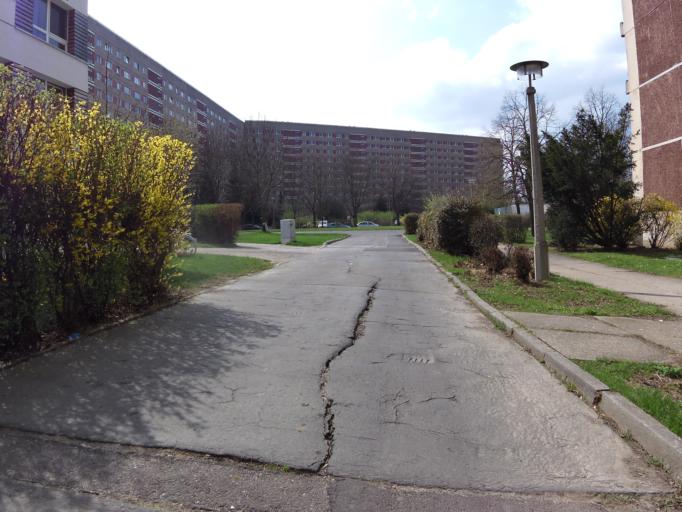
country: DE
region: Saxony
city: Markranstadt
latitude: 51.3173
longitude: 12.2861
